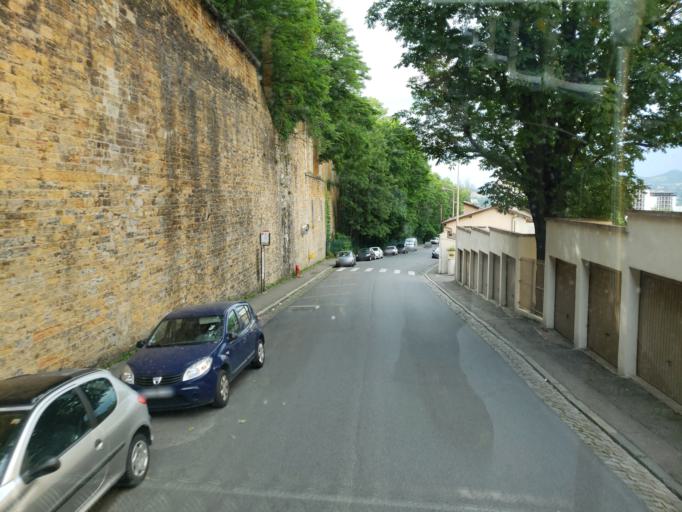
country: FR
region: Rhone-Alpes
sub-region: Departement du Rhone
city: Tassin-la-Demi-Lune
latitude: 45.7656
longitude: 4.8103
